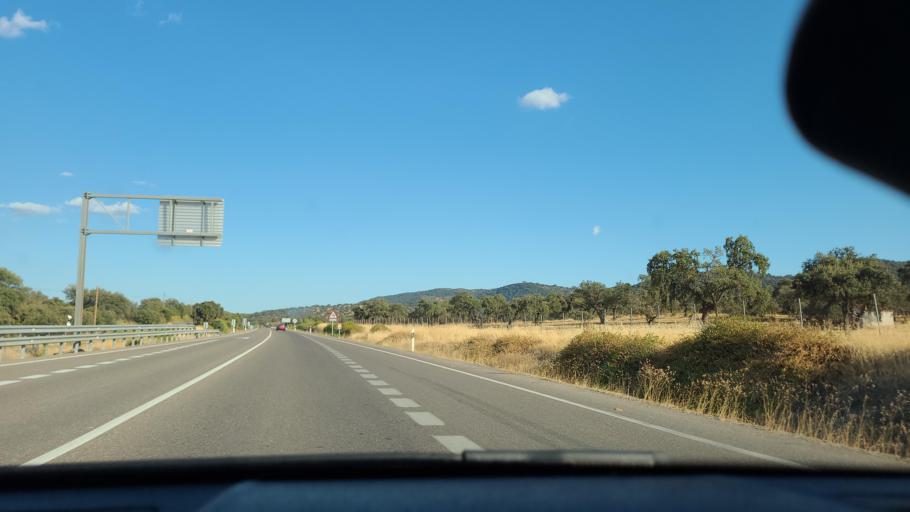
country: ES
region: Andalusia
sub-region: Province of Cordoba
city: Belmez
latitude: 38.2121
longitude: -5.1381
